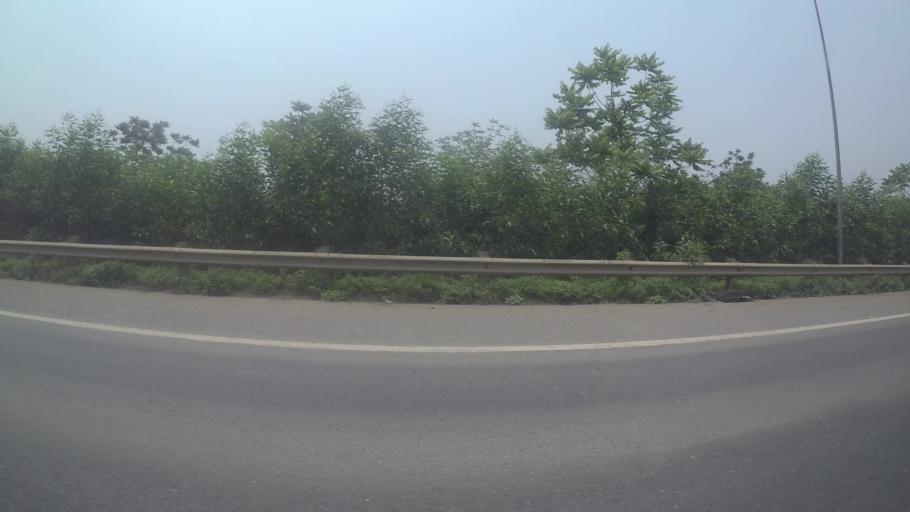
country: VN
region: Ha Noi
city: Lien Quan
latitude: 20.9890
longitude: 105.5685
